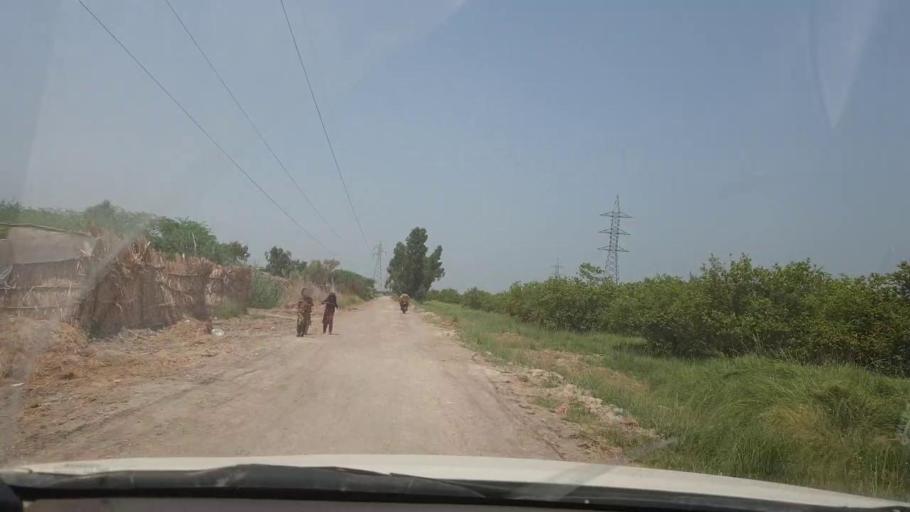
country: PK
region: Sindh
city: Lakhi
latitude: 27.8608
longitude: 68.6991
